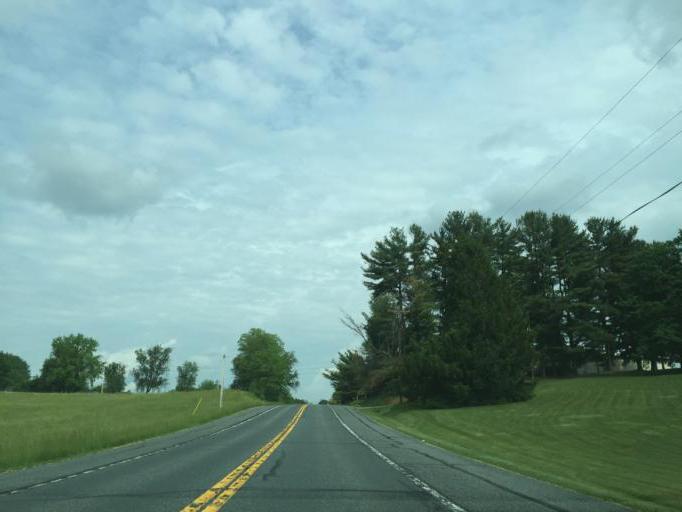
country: US
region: Maryland
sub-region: Harford County
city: Jarrettsville
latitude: 39.6656
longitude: -76.4350
